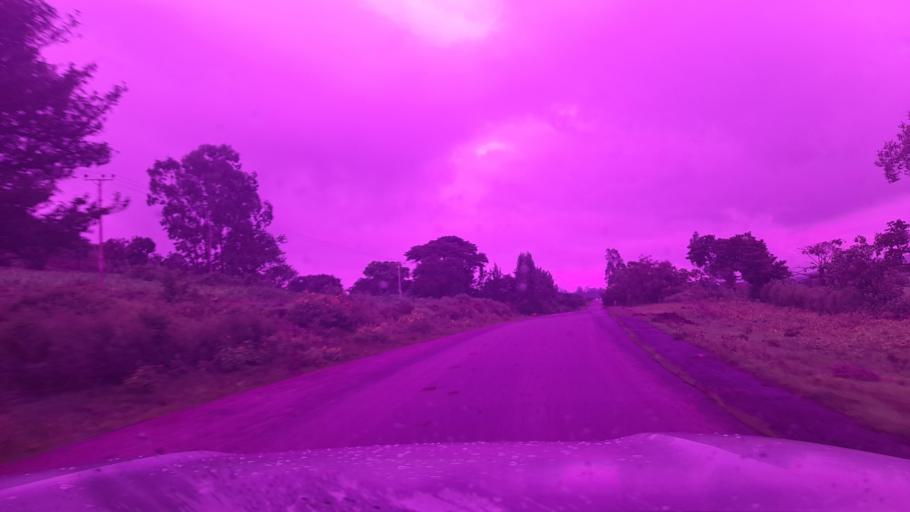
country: ET
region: Oromiya
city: Jima
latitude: 7.7827
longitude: 37.3424
